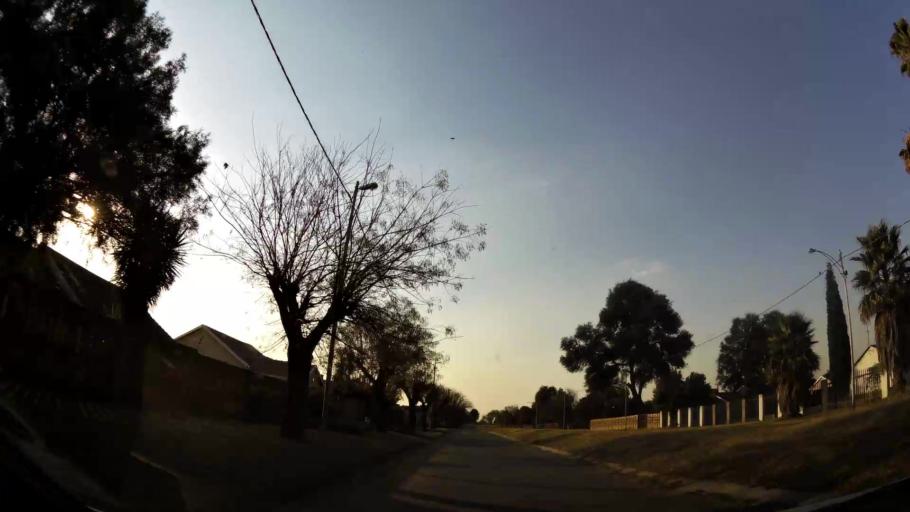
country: ZA
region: Gauteng
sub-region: Ekurhuleni Metropolitan Municipality
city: Springs
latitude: -26.2593
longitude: 28.3945
